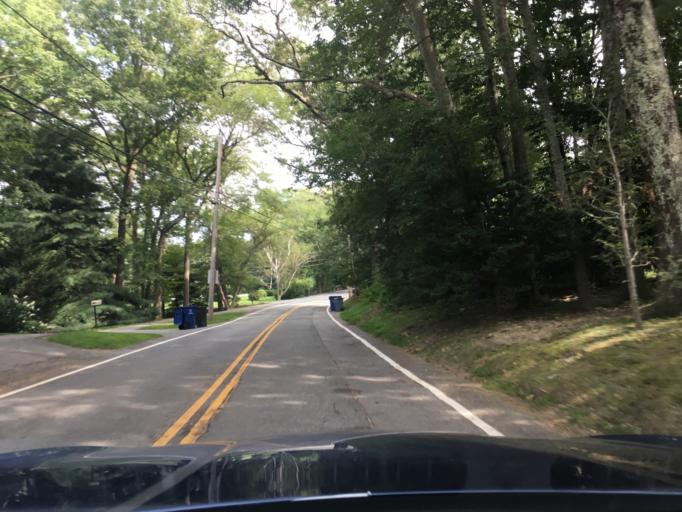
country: US
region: Rhode Island
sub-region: Kent County
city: East Greenwich
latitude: 41.6583
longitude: -71.4679
